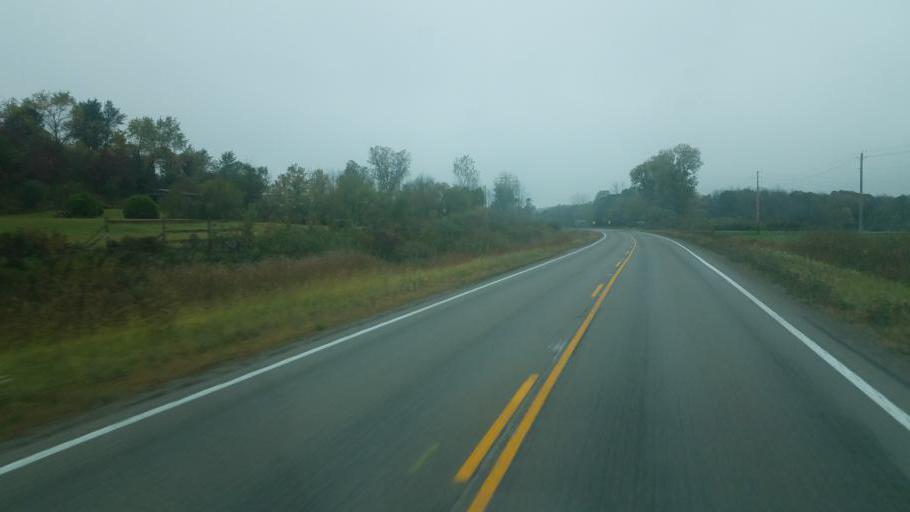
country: US
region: Ohio
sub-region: Sandusky County
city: Bellville
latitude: 40.5597
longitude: -82.4716
